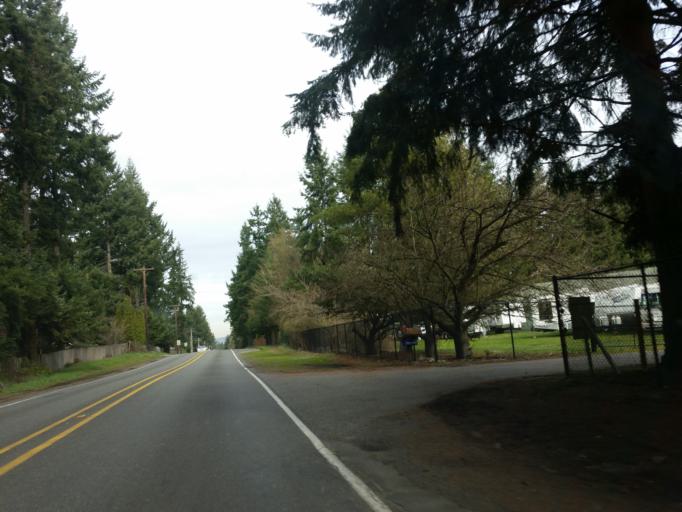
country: US
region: Washington
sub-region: Pierce County
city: South Hill
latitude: 47.1604
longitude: -122.2559
